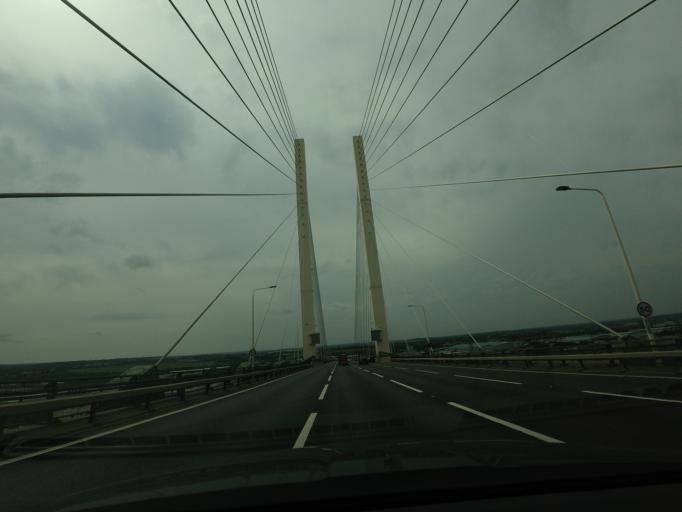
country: GB
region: England
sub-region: Kent
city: Stone
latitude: 51.4636
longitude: 0.2580
